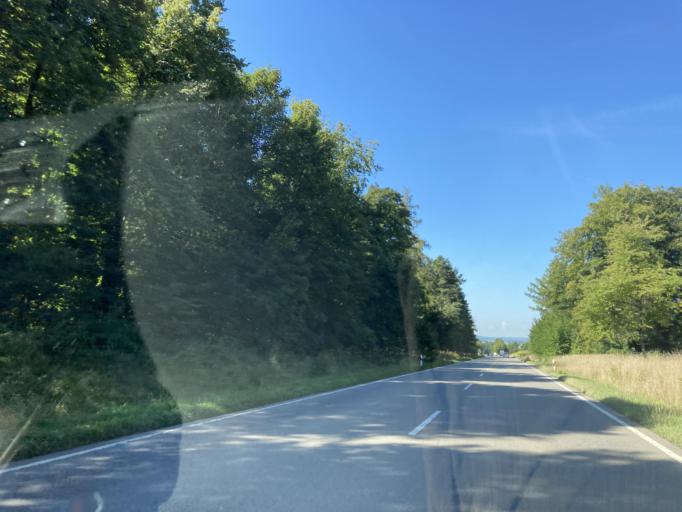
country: DE
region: Baden-Wuerttemberg
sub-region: Tuebingen Region
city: Betzenweiler
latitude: 48.1388
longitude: 9.5579
